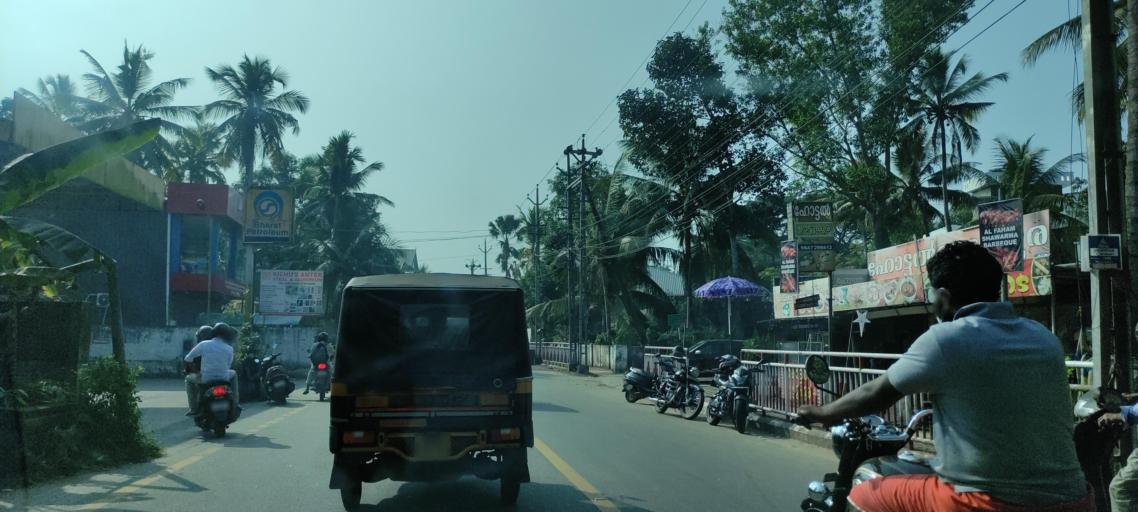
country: IN
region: Kerala
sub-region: Kottayam
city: Changanacheri
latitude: 9.3672
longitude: 76.4805
